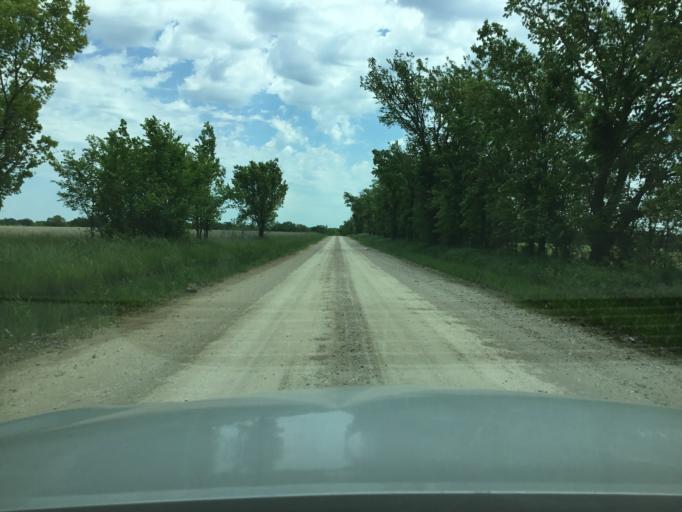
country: US
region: Kansas
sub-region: Montgomery County
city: Independence
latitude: 37.0951
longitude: -95.7996
